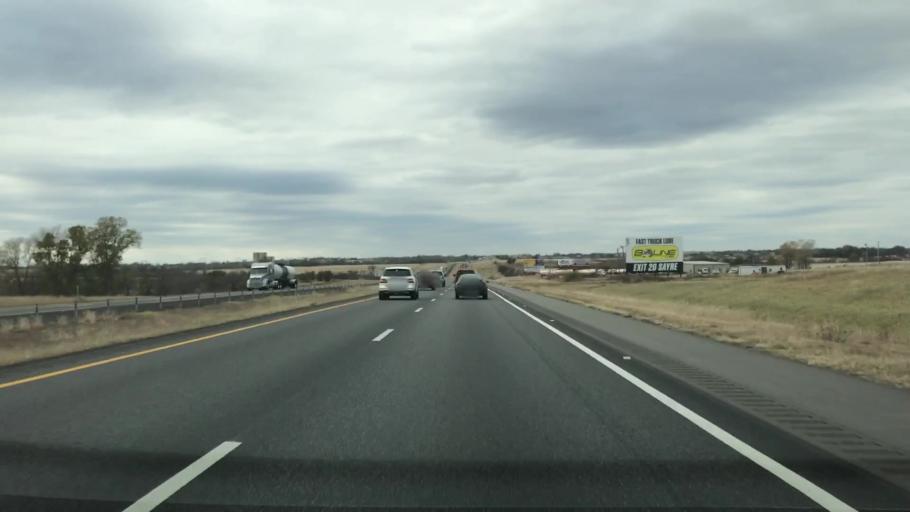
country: US
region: Oklahoma
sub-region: Beckham County
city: Elk City
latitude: 35.3857
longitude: -99.4243
